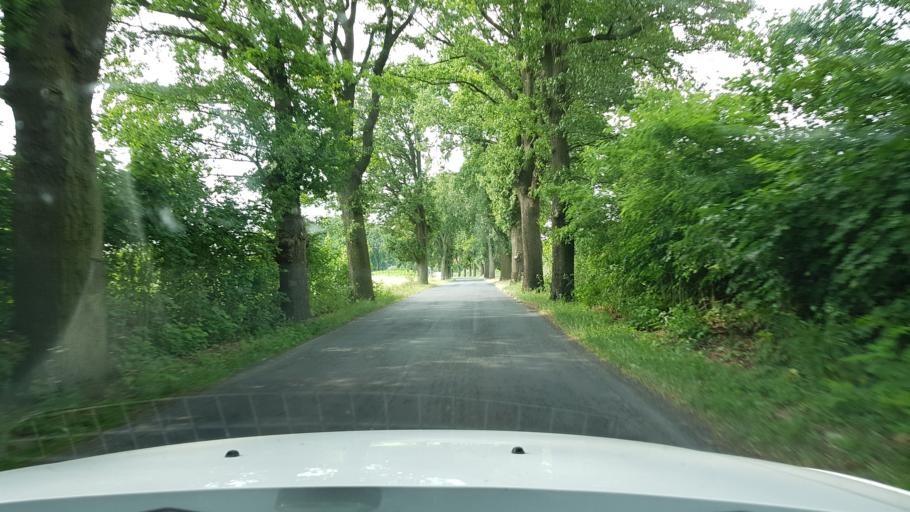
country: PL
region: West Pomeranian Voivodeship
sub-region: Powiat gryfinski
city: Moryn
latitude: 52.9134
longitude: 14.3670
